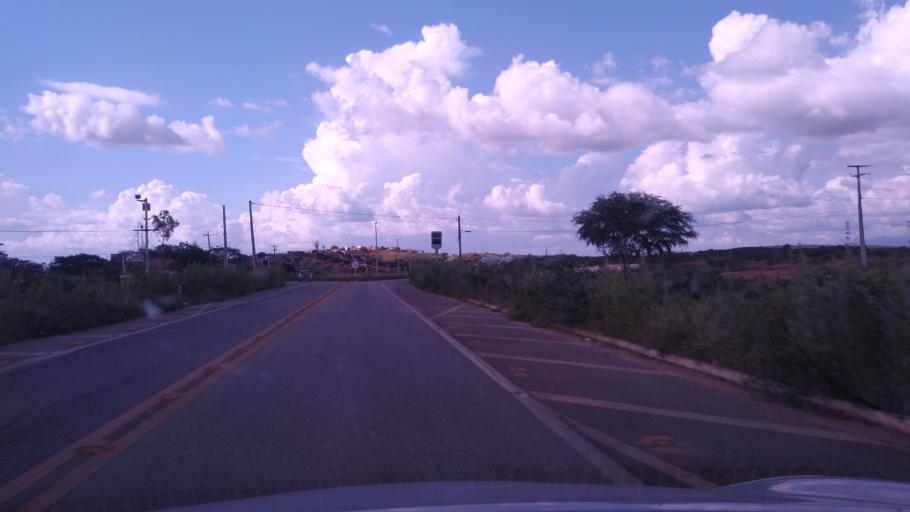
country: BR
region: Ceara
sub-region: Caninde
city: Caninde
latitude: -4.3805
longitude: -39.3099
